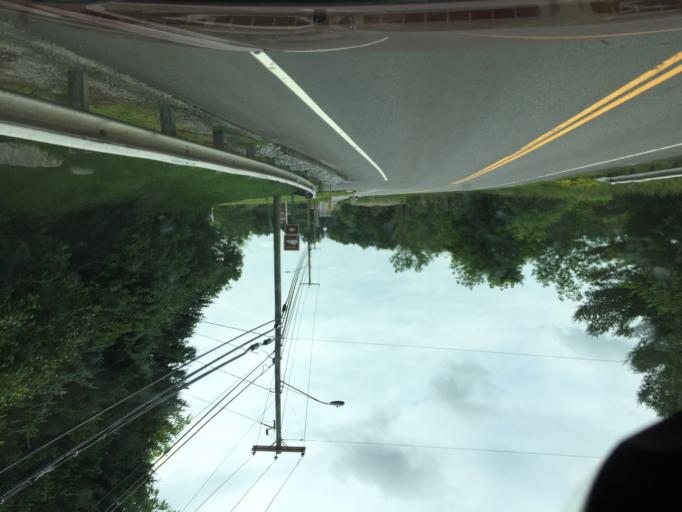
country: US
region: Connecticut
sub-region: Litchfield County
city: West Torrington
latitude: 41.8311
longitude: -73.2390
